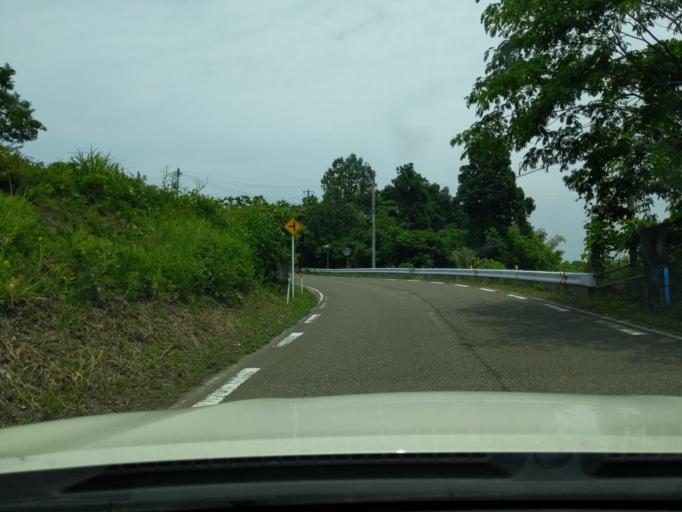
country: JP
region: Niigata
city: Kashiwazaki
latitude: 37.3484
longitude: 138.5497
